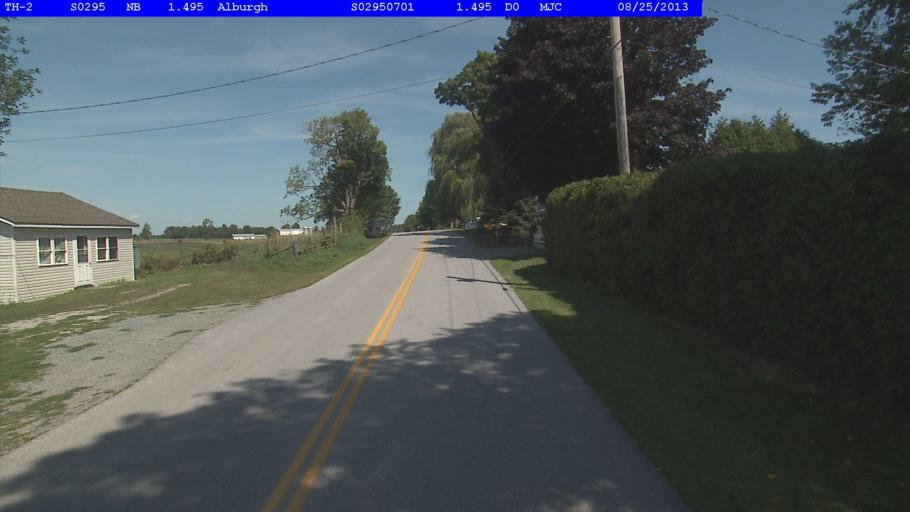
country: US
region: Vermont
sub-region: Franklin County
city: Swanton
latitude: 44.9947
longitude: -73.2214
